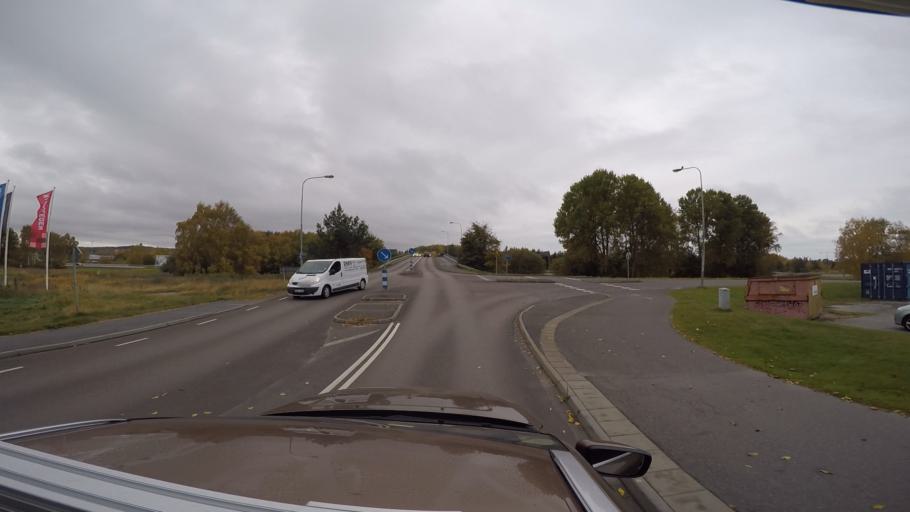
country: SE
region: Vaestra Goetaland
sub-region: Goteborg
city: Majorna
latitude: 57.6471
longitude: 11.9395
